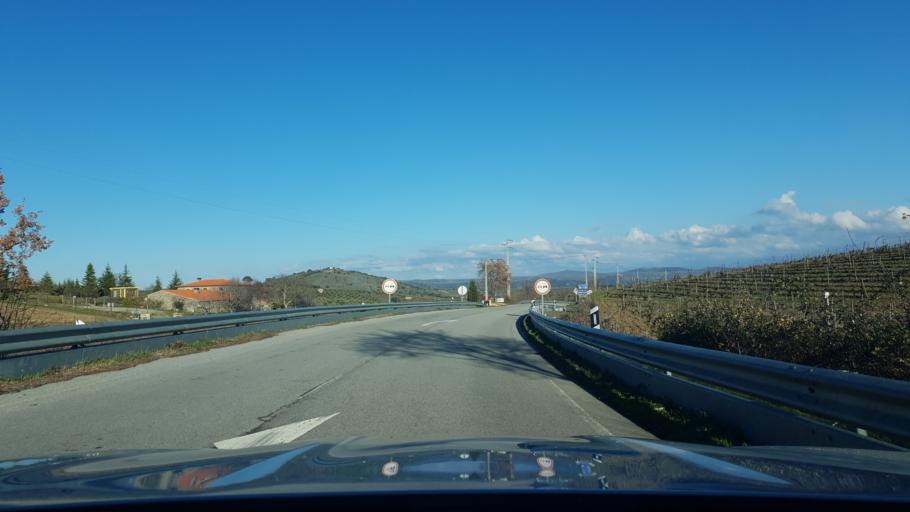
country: PT
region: Braganca
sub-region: Freixo de Espada A Cinta
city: Freixo de Espada a Cinta
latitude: 41.0938
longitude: -6.8290
